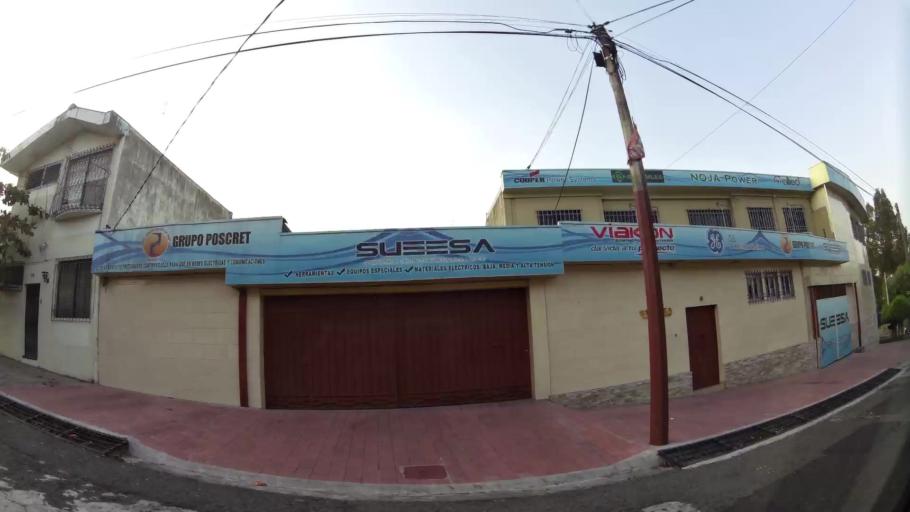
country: SV
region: La Libertad
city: Antiguo Cuscatlan
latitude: 13.7010
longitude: -89.2468
